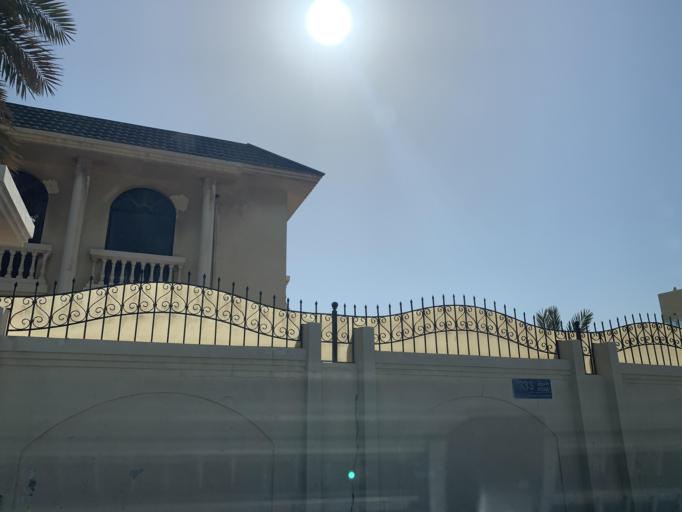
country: BH
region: Manama
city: Manama
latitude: 26.2013
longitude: 50.5684
